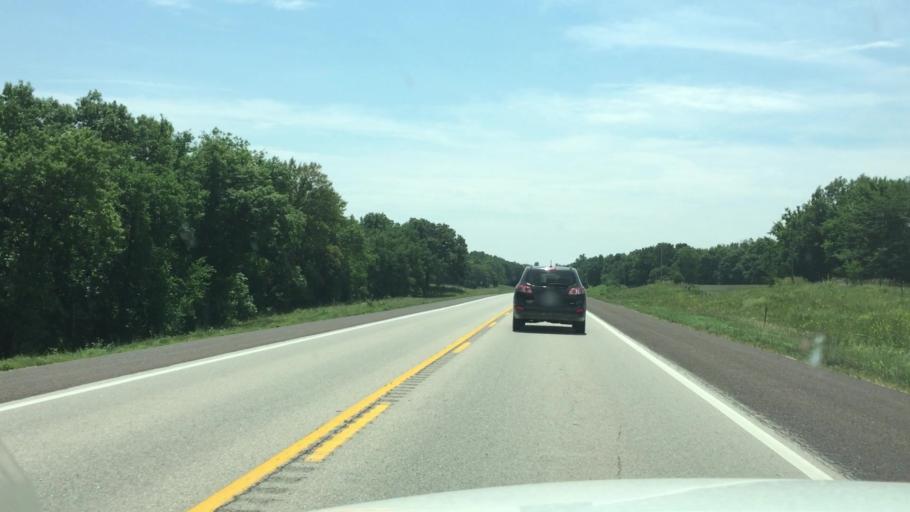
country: US
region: Kansas
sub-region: Jackson County
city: Holton
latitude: 39.5396
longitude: -95.7483
